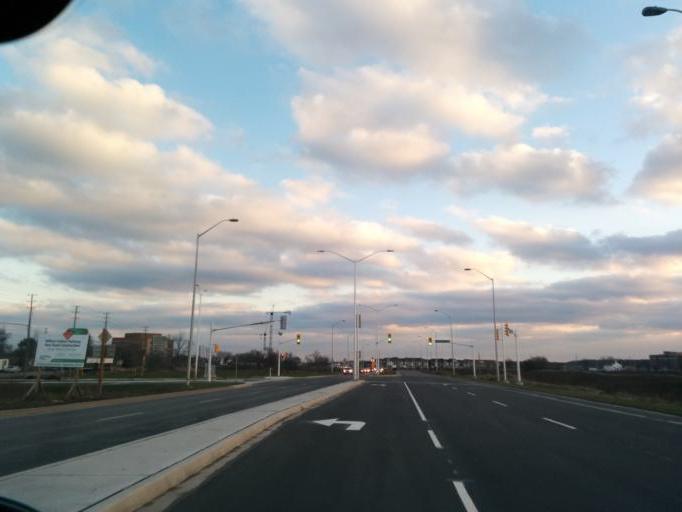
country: CA
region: Ontario
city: Burlington
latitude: 43.4384
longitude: -79.7813
